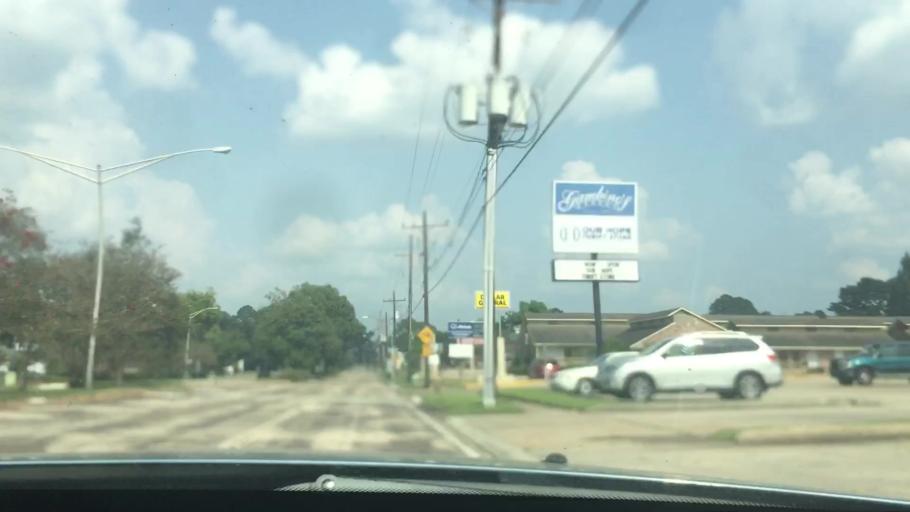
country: US
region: Louisiana
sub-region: East Baton Rouge Parish
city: Westminster
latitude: 30.4423
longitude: -91.1045
